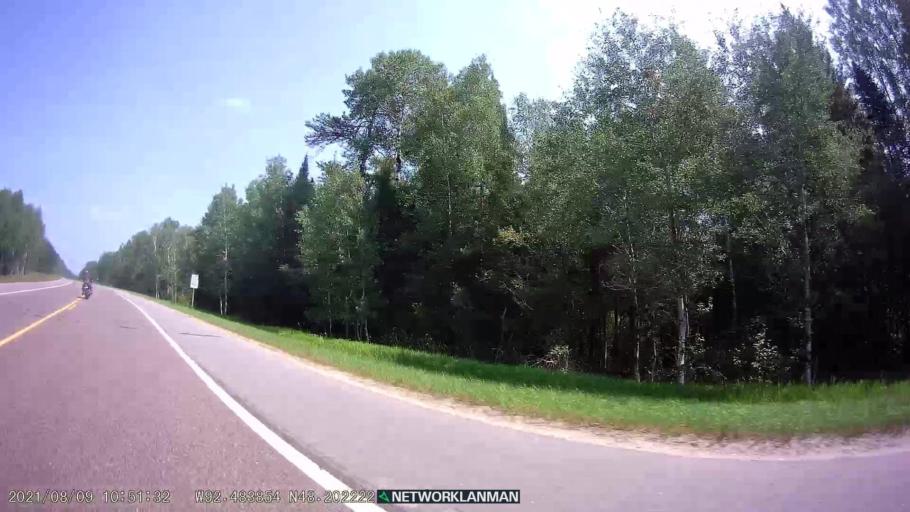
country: US
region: Minnesota
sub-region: Saint Louis County
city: Parkville
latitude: 48.2022
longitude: -92.4836
